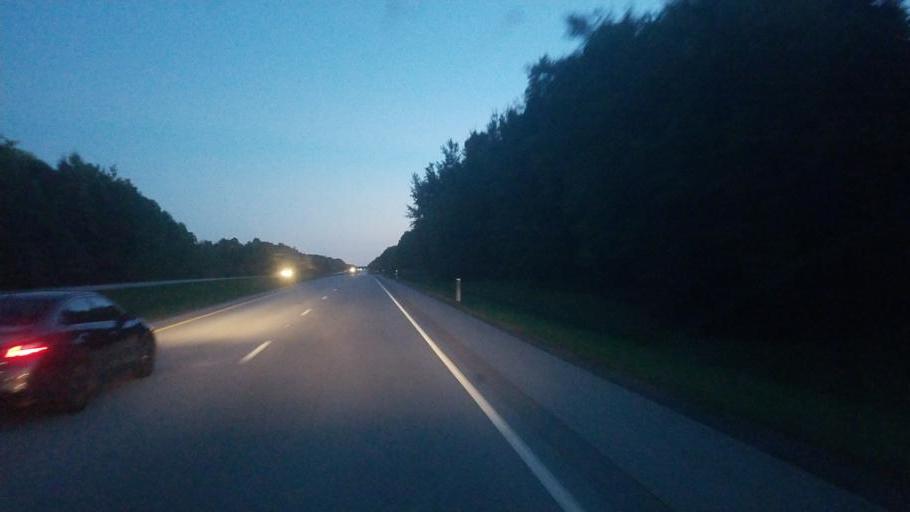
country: US
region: Ohio
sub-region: Ashtabula County
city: Jefferson
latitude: 41.6608
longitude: -80.7137
